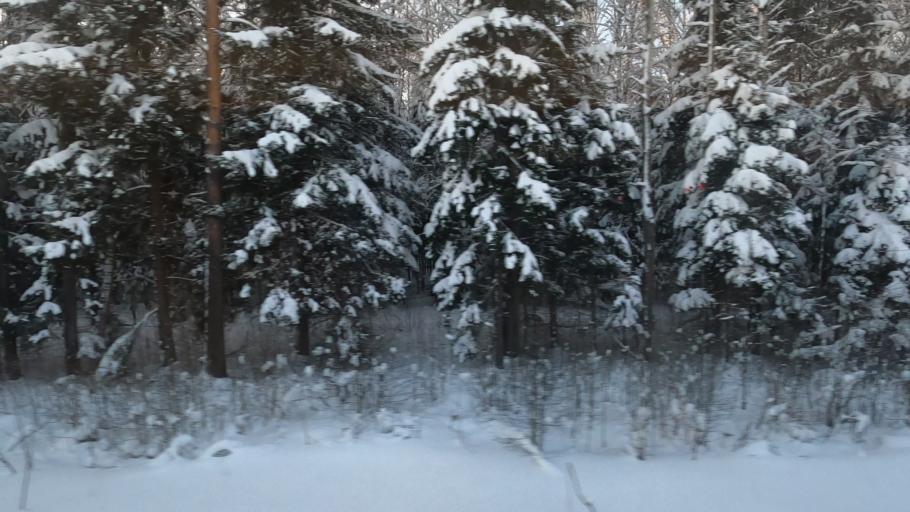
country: RU
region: Moskovskaya
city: Taldom
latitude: 56.6582
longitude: 37.5677
